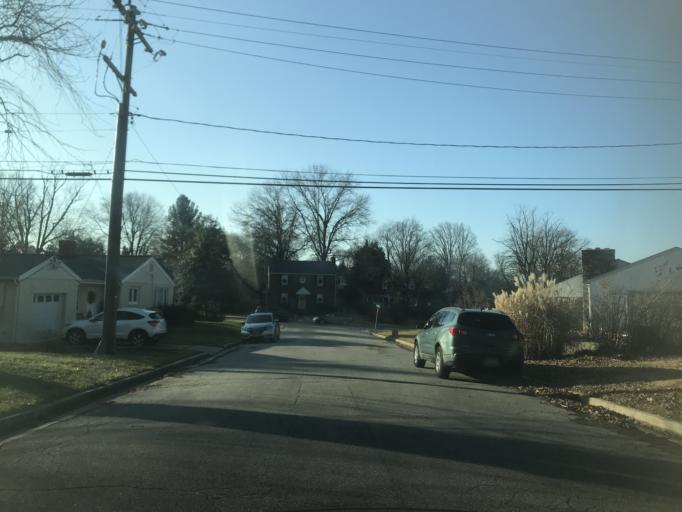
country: US
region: Maryland
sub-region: Baltimore County
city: Towson
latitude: 39.3888
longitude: -76.5937
